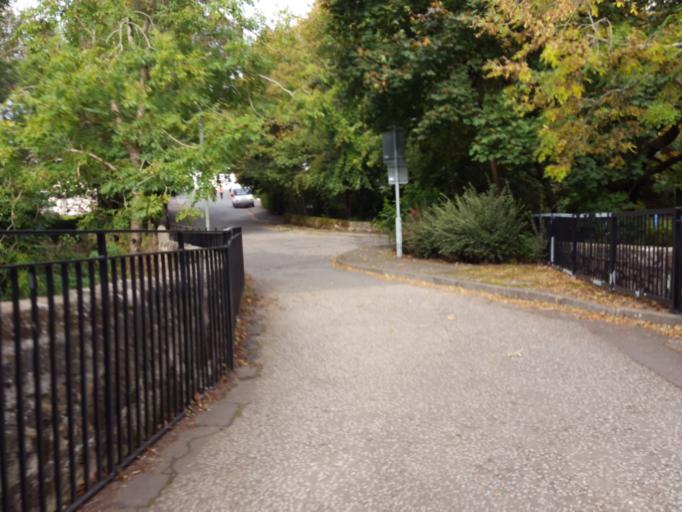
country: GB
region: Scotland
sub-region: West Lothian
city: Livingston
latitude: 55.8846
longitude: -3.5390
